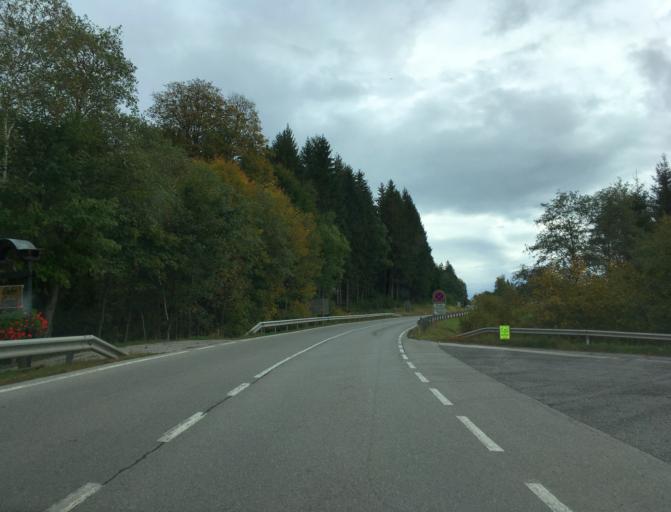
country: AT
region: Lower Austria
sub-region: Politischer Bezirk Neunkirchen
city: Thomasberg
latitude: 47.5464
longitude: 16.1465
